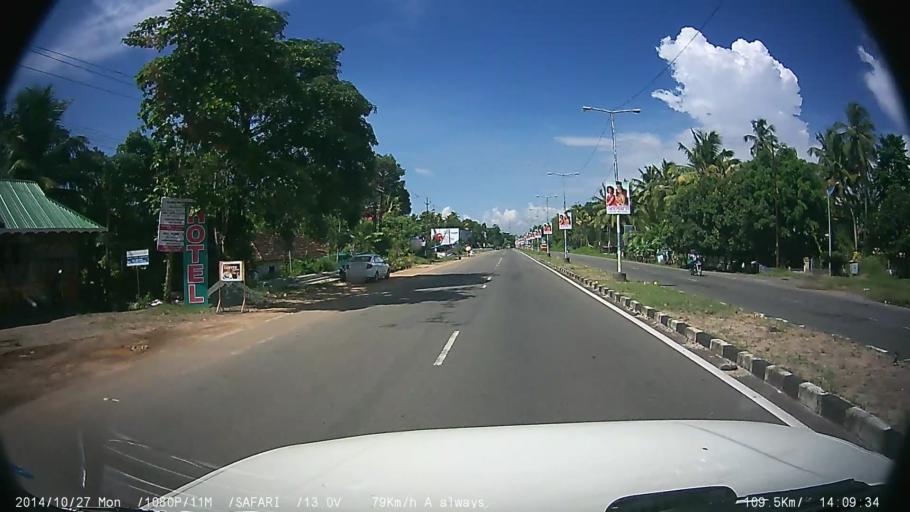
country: IN
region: Kerala
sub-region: Alappuzha
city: Kutiatodu
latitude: 9.7713
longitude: 76.3182
